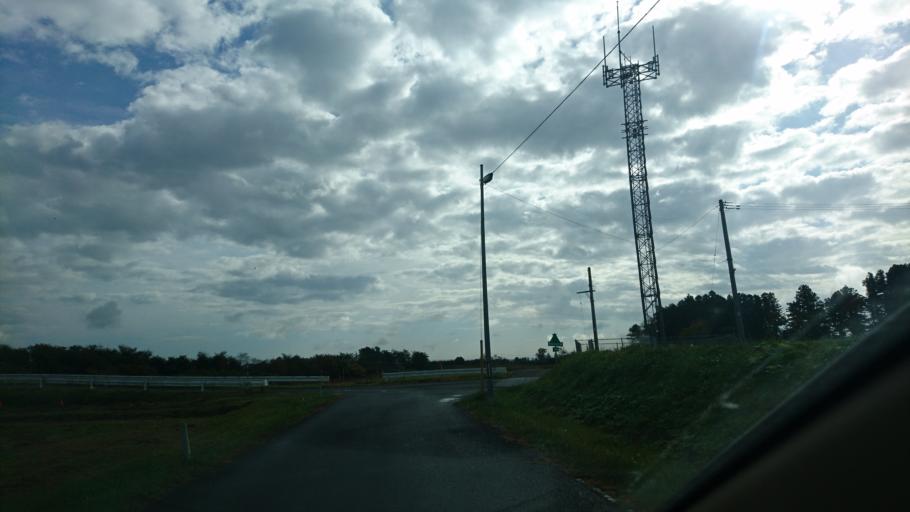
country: JP
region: Iwate
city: Ichinoseki
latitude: 38.7849
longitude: 141.0113
